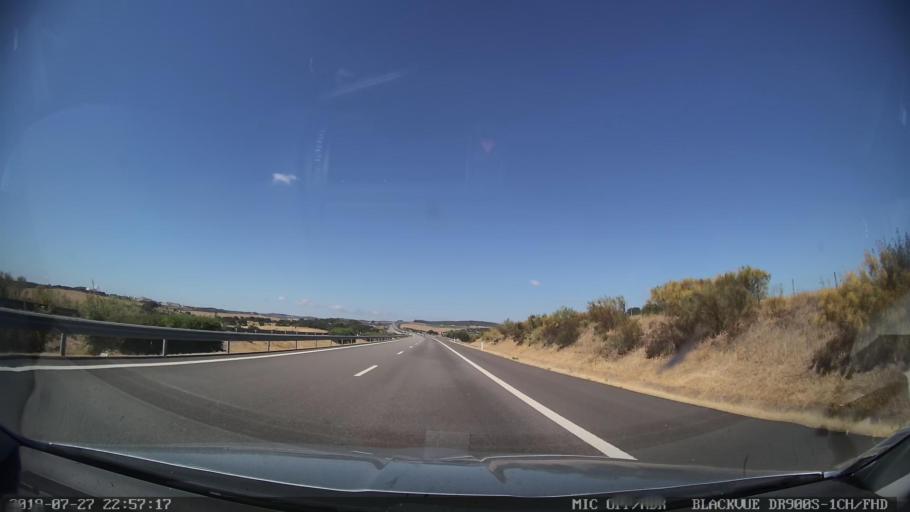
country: PT
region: Evora
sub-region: Borba
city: Borba
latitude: 38.8336
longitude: -7.4147
